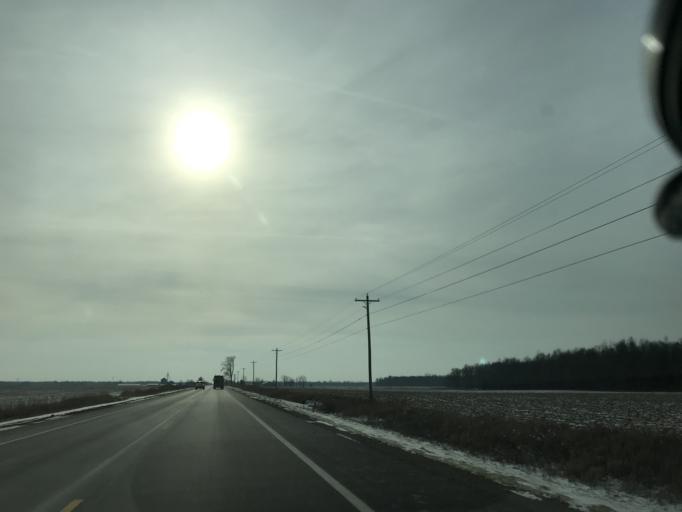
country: US
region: Michigan
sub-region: Ionia County
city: Lake Odessa
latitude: 42.8350
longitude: -85.0749
